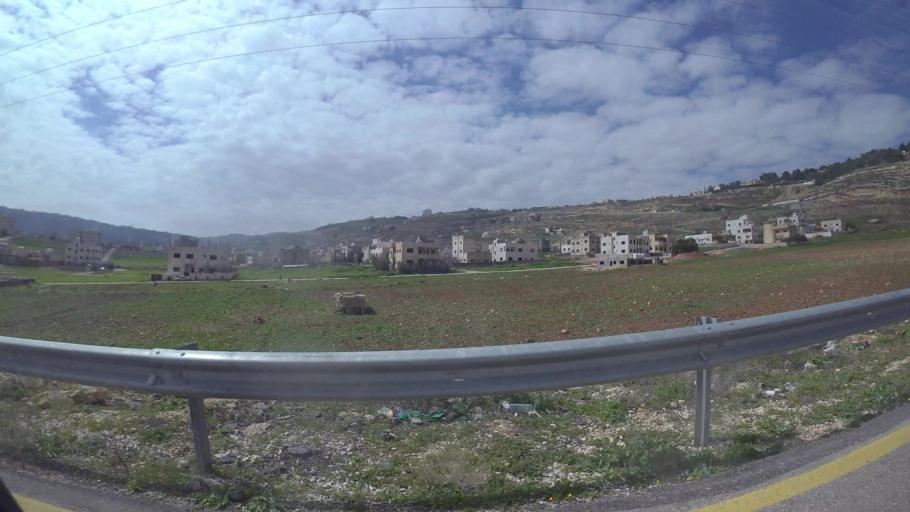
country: JO
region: Amman
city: Al Jubayhah
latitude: 32.0623
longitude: 35.8093
